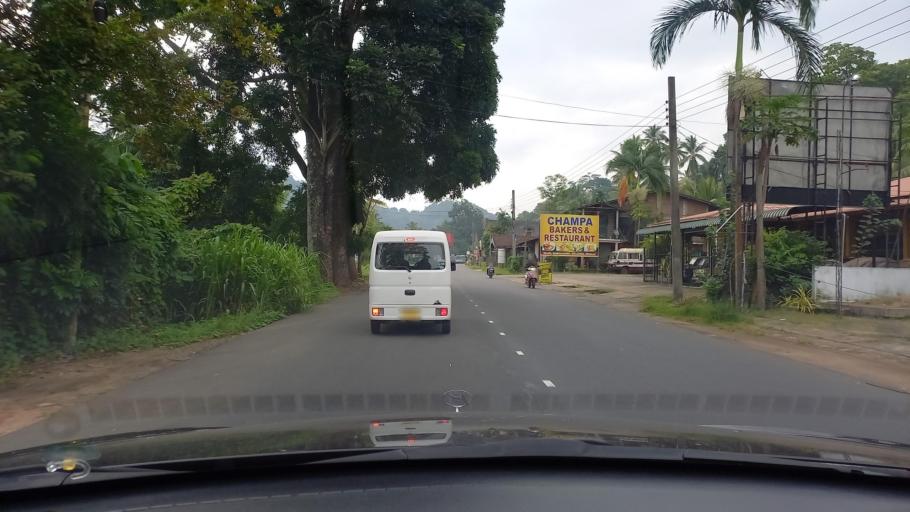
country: LK
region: Central
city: Kadugannawa
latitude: 7.2569
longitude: 80.4058
